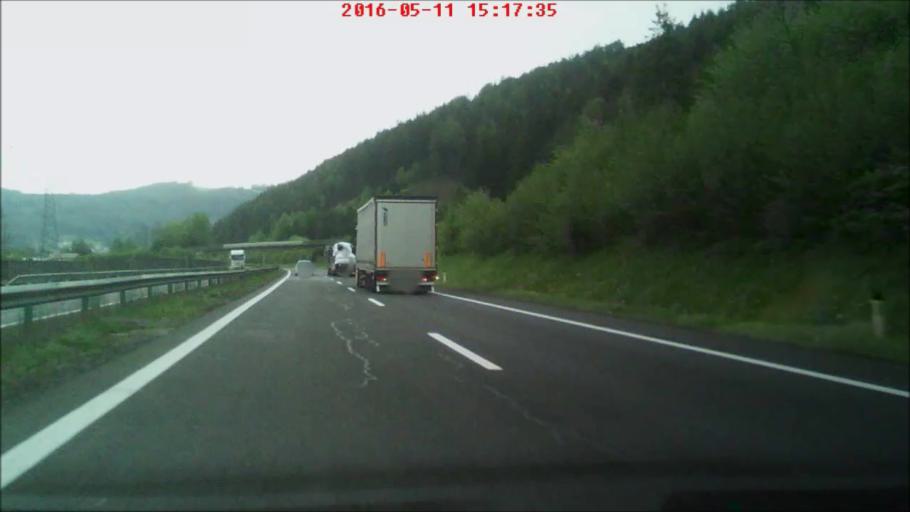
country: AT
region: Styria
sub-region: Politischer Bezirk Leoben
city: Traboch
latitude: 47.3754
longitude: 14.9592
